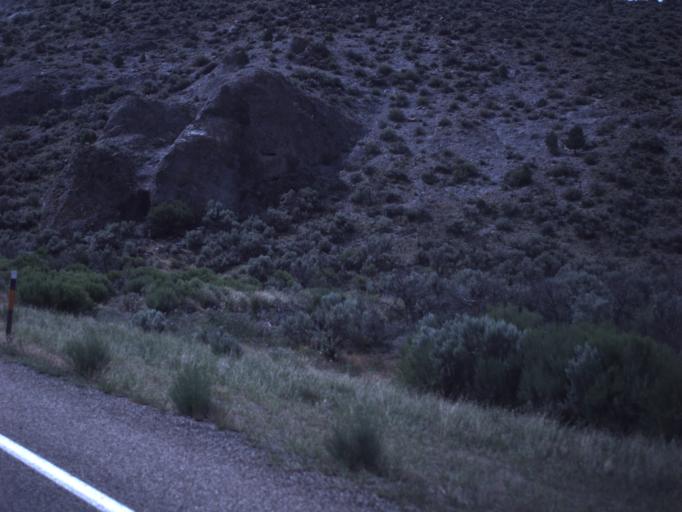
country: US
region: Utah
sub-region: Garfield County
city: Panguitch
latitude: 37.9701
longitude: -112.4391
